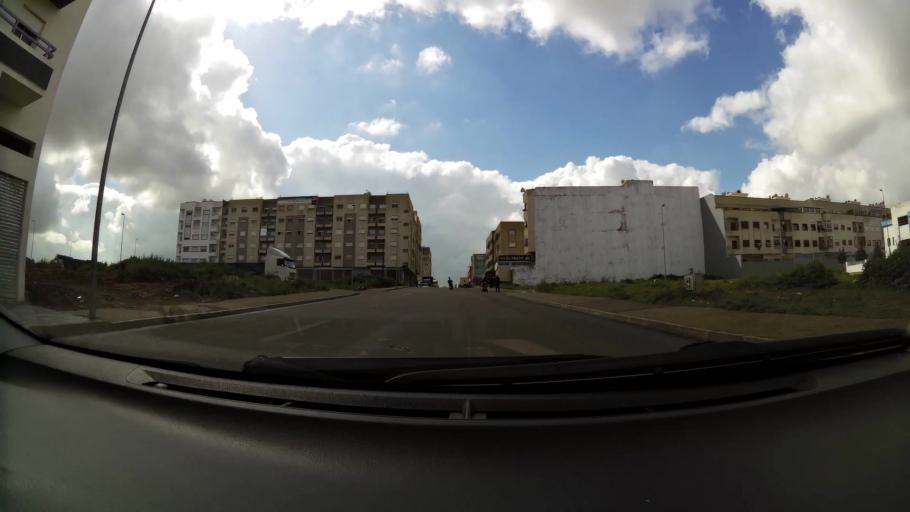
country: MA
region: Grand Casablanca
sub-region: Mediouna
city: Tit Mellil
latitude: 33.5473
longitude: -7.4831
